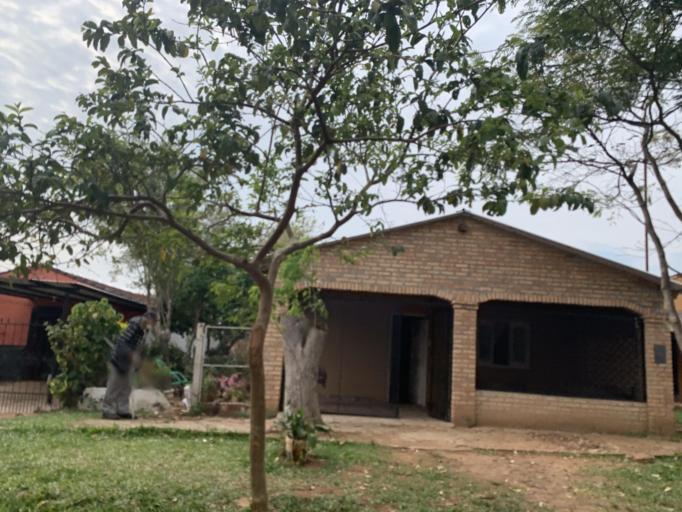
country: PY
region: Misiones
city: San Juan Bautista
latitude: -26.6604
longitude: -57.1506
